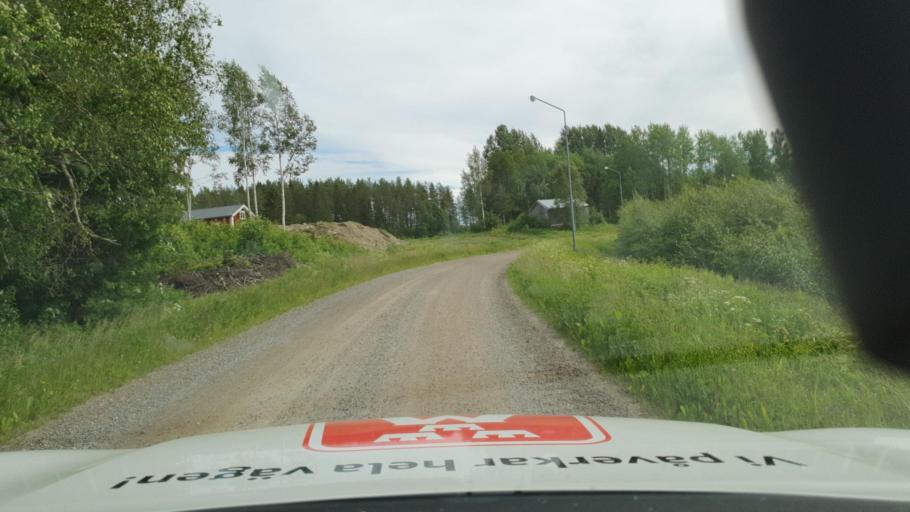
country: SE
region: Vaesterbotten
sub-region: Robertsfors Kommun
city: Robertsfors
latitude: 64.3851
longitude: 21.0400
